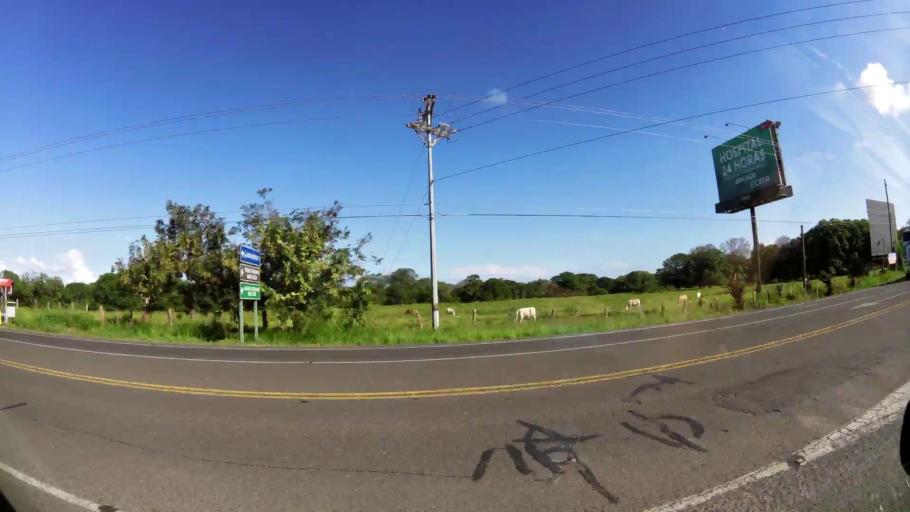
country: CR
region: Guanacaste
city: Sardinal
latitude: 10.5578
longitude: -85.5917
